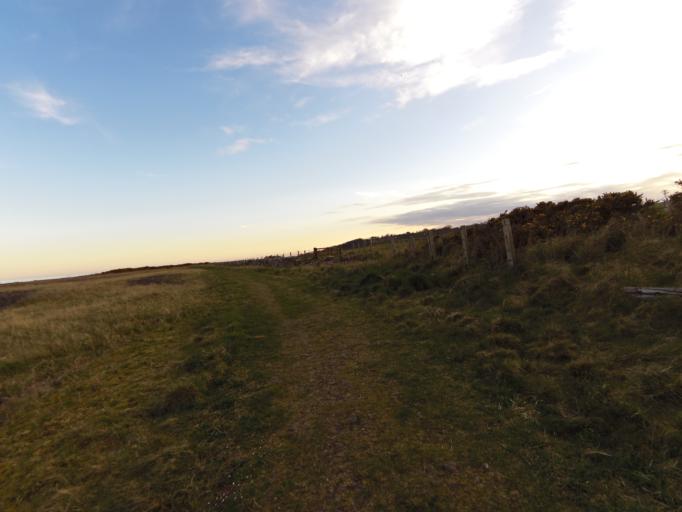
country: GB
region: Scotland
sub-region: Aberdeenshire
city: Inverbervie
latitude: 56.8148
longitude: -2.3029
